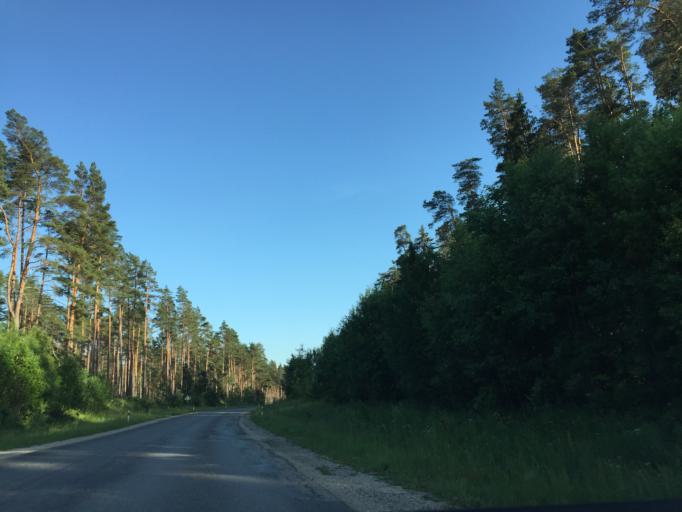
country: LV
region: Tukuma Rajons
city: Tukums
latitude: 57.0051
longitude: 23.1438
